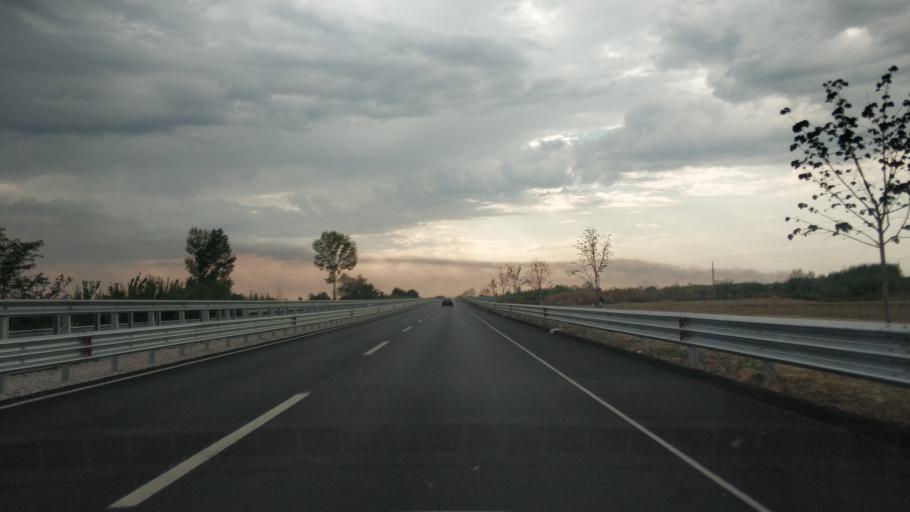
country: AL
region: Fier
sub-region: Rrethi i Fierit
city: Dermenas
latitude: 40.7493
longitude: 19.5293
